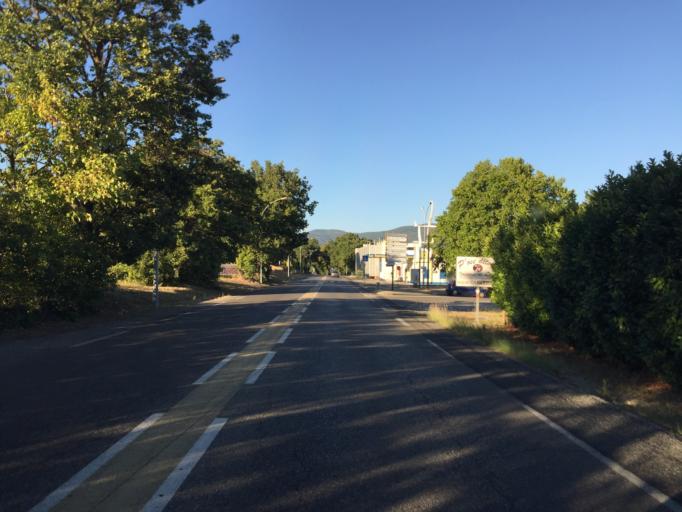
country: FR
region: Provence-Alpes-Cote d'Azur
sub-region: Departement des Alpes-de-Haute-Provence
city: Les Mees
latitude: 44.0686
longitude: 5.9842
